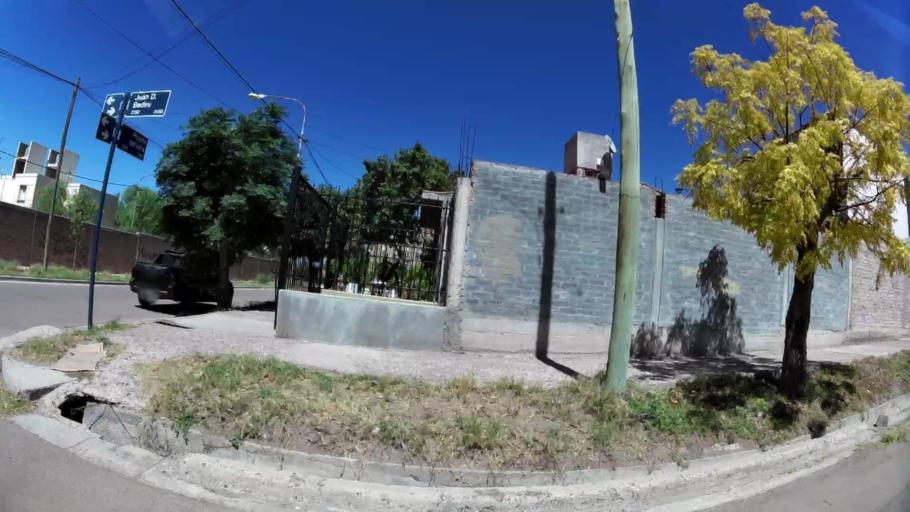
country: AR
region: Mendoza
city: Las Heras
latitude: -32.8523
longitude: -68.8637
